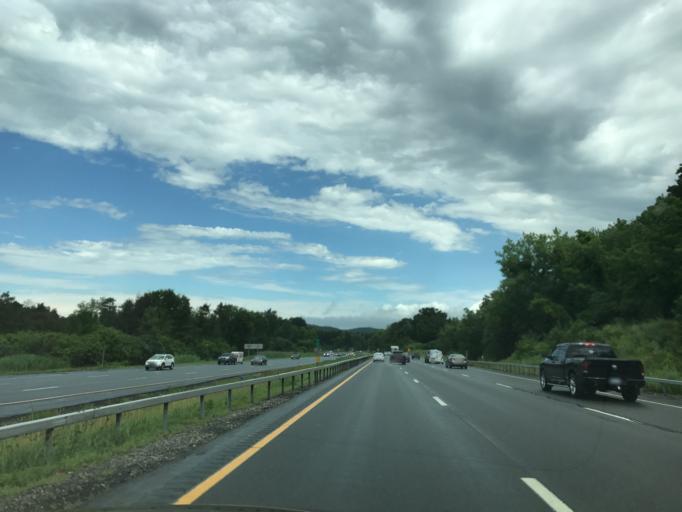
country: US
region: New York
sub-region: Albany County
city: Cohoes
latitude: 42.7821
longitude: -73.7587
